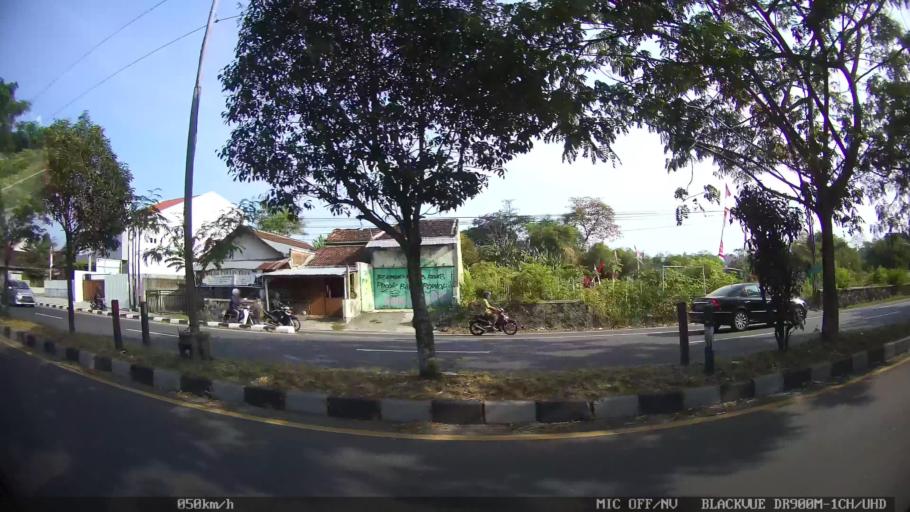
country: ID
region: Daerah Istimewa Yogyakarta
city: Kasihan
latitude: -7.8256
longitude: 110.3385
